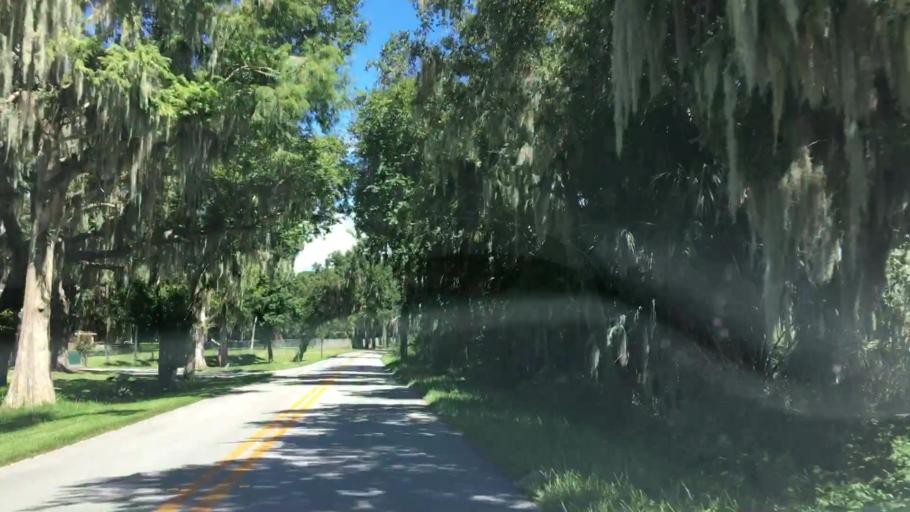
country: US
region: Florida
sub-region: Volusia County
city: Deltona
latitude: 28.8665
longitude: -81.2643
